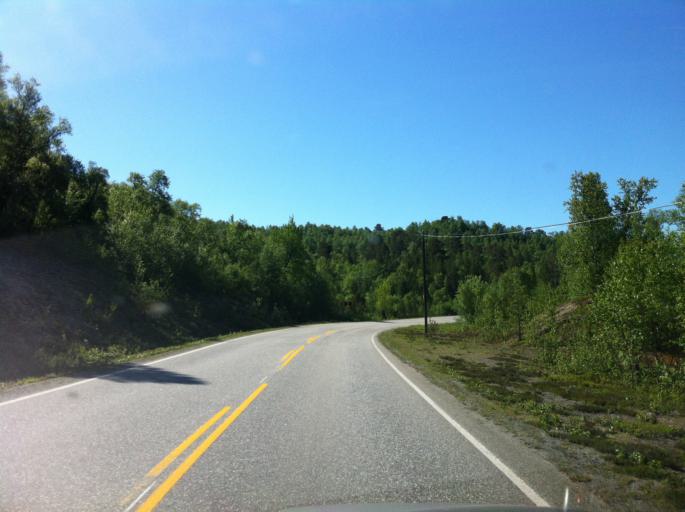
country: NO
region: Sor-Trondelag
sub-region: Roros
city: Roros
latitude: 62.6159
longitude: 11.8457
